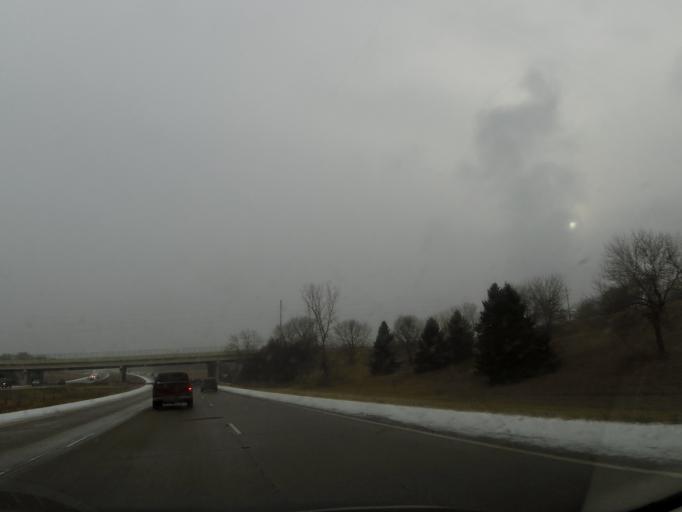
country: US
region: Minnesota
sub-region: Dakota County
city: Eagan
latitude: 44.7920
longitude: -93.2221
